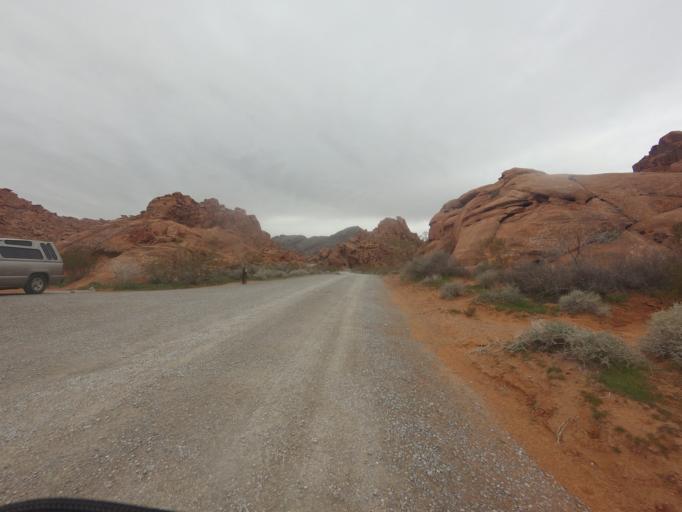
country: US
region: Nevada
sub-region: Clark County
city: Moapa Valley
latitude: 36.4174
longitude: -114.5528
